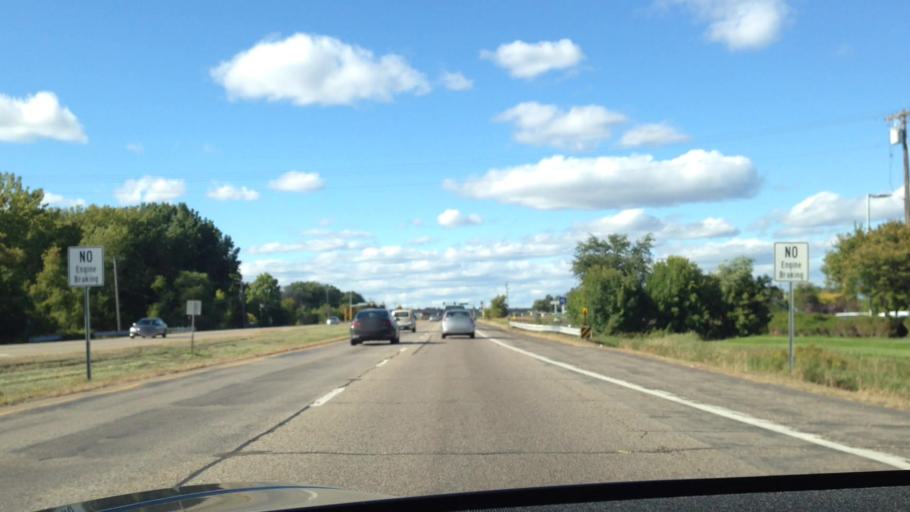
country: US
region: Minnesota
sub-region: Hennepin County
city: Osseo
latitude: 45.0982
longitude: -93.3868
